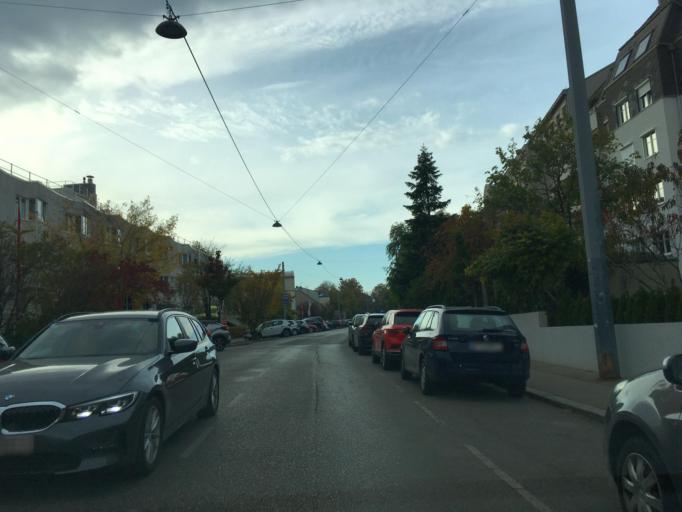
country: AT
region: Vienna
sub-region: Wien Stadt
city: Vienna
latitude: 48.2437
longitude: 16.3323
